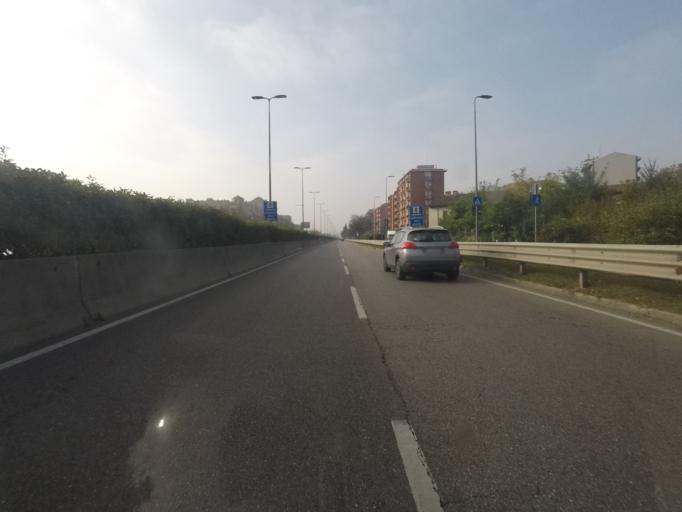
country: IT
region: Lombardy
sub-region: Citta metropolitana di Milano
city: Cologno Monzese
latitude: 45.5112
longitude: 9.2556
